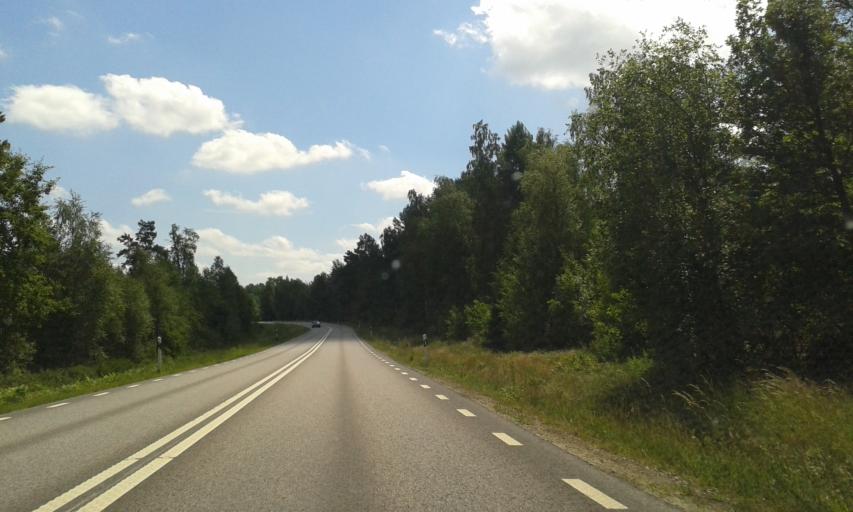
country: SE
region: Kronoberg
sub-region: Vaxjo Kommun
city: Vaexjoe
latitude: 56.8330
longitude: 14.8656
